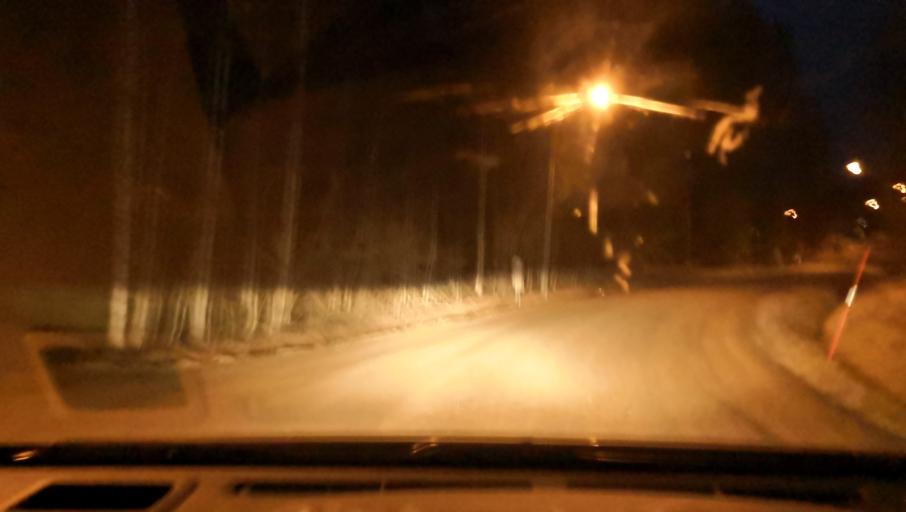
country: SE
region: Vaestmanland
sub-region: Skinnskattebergs Kommun
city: Skinnskatteberg
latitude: 59.6662
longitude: 15.5279
